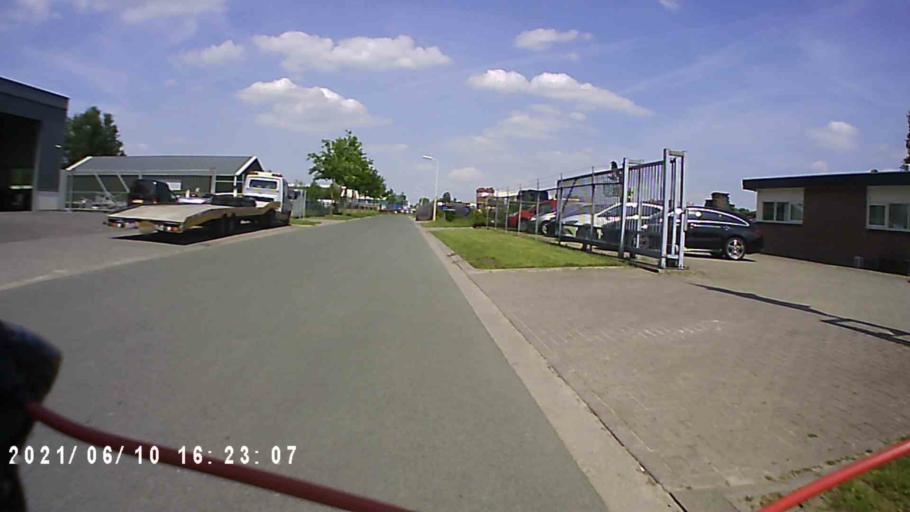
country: NL
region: Friesland
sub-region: Gemeente Achtkarspelen
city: Kootstertille
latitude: 53.2172
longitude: 6.1042
